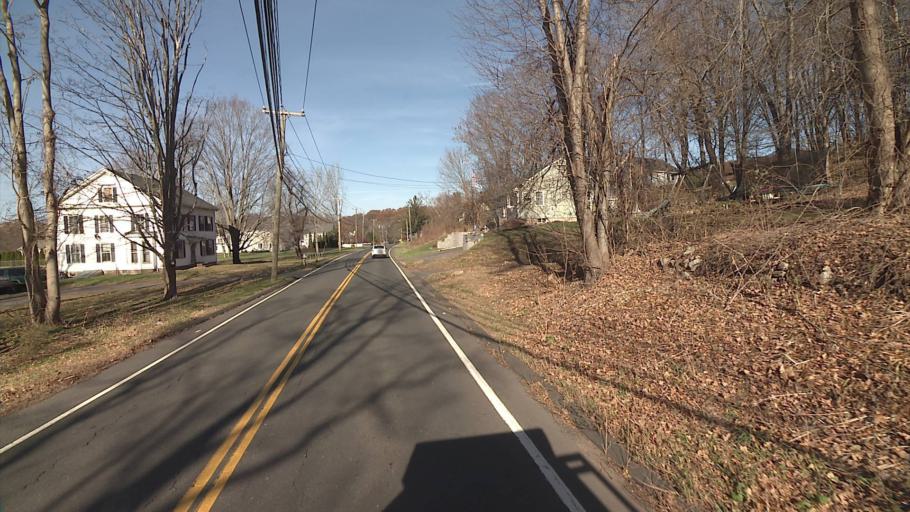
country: US
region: Connecticut
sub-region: Middlesex County
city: Cromwell
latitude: 41.6226
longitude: -72.6011
